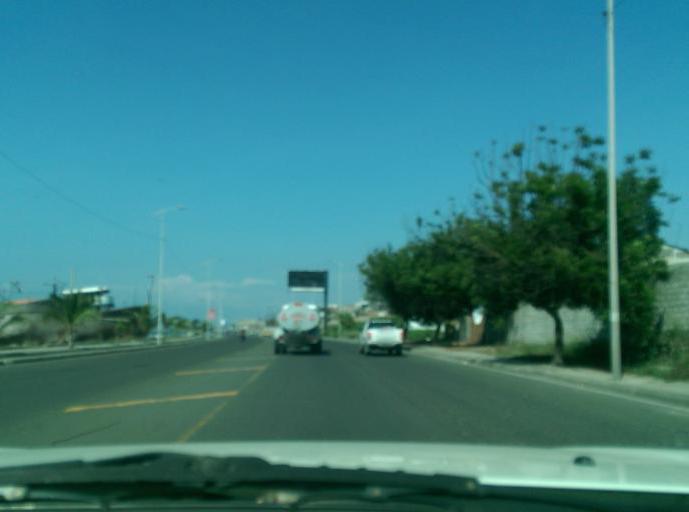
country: EC
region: Manabi
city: Manta
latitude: -0.9505
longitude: -80.7075
